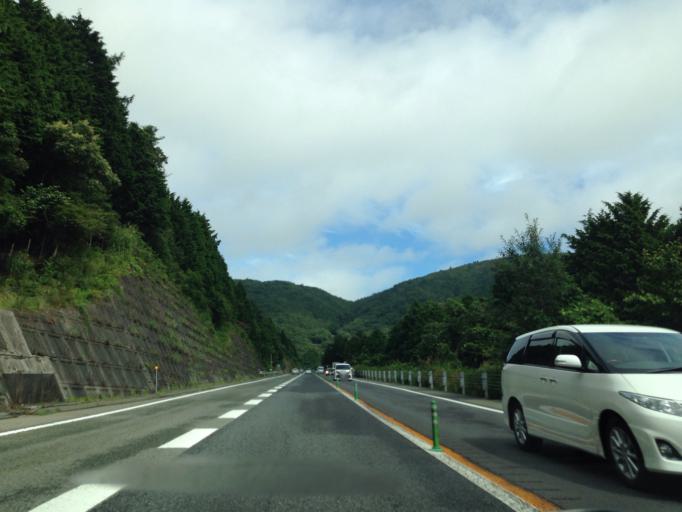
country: JP
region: Shizuoka
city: Gotemba
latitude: 35.3738
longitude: 138.8484
